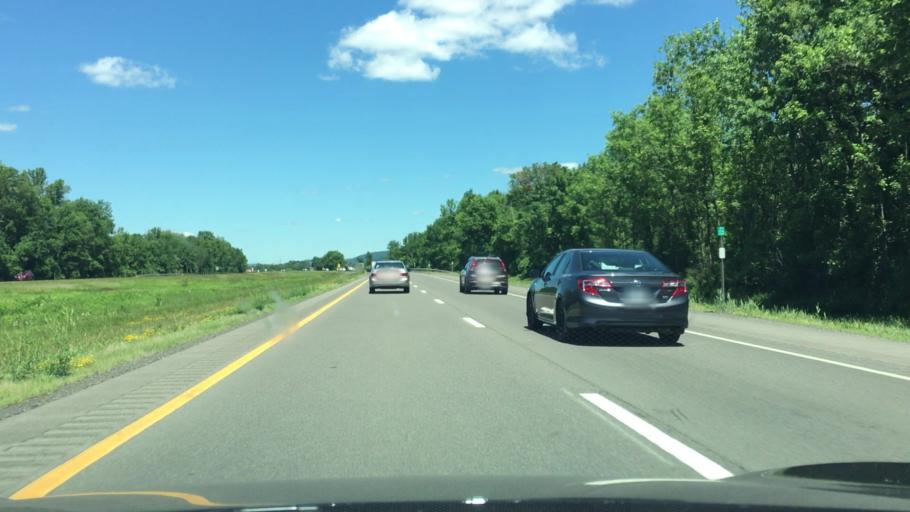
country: US
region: New York
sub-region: Cortland County
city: Homer
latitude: 42.6661
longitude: -76.1715
